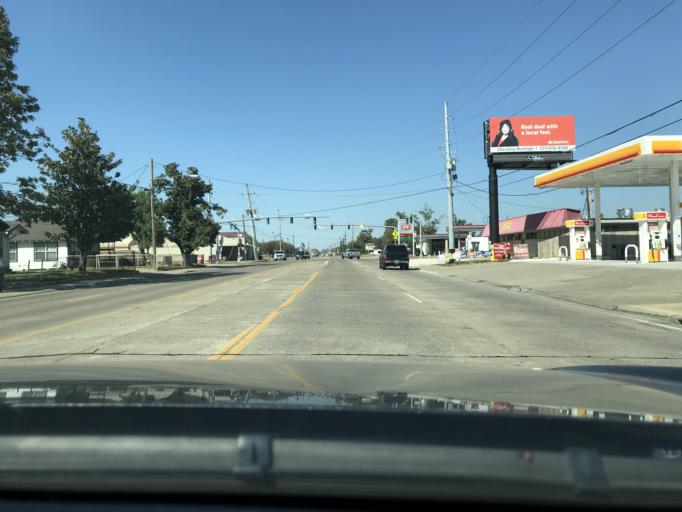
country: US
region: Louisiana
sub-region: Calcasieu Parish
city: Westlake
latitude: 30.2469
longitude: -93.2581
